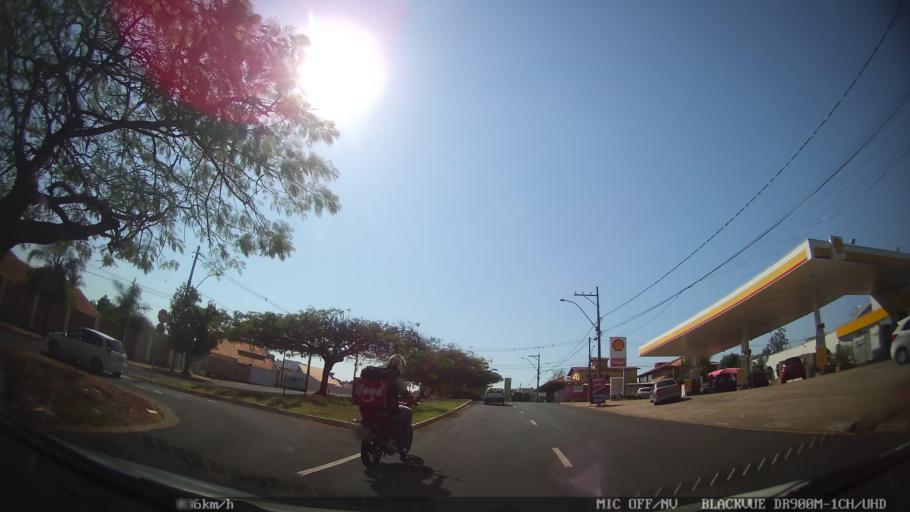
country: BR
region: Sao Paulo
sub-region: Ribeirao Preto
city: Ribeirao Preto
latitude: -21.2114
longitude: -47.7731
